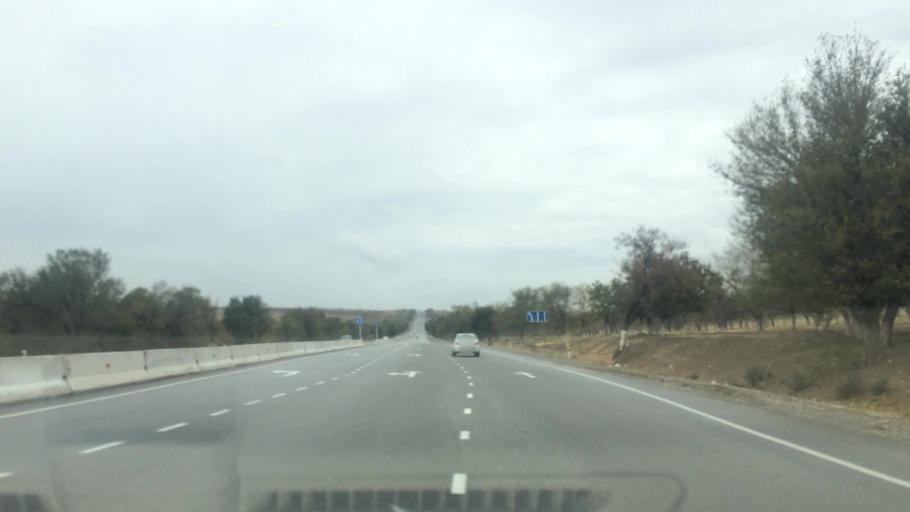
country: UZ
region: Samarqand
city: Bulung'ur
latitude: 39.8776
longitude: 67.4832
